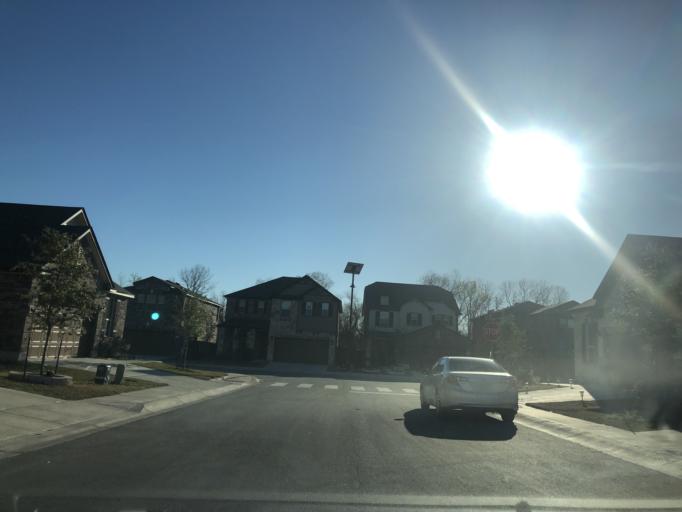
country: US
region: Texas
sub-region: Travis County
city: Windemere
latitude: 30.4720
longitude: -97.6582
